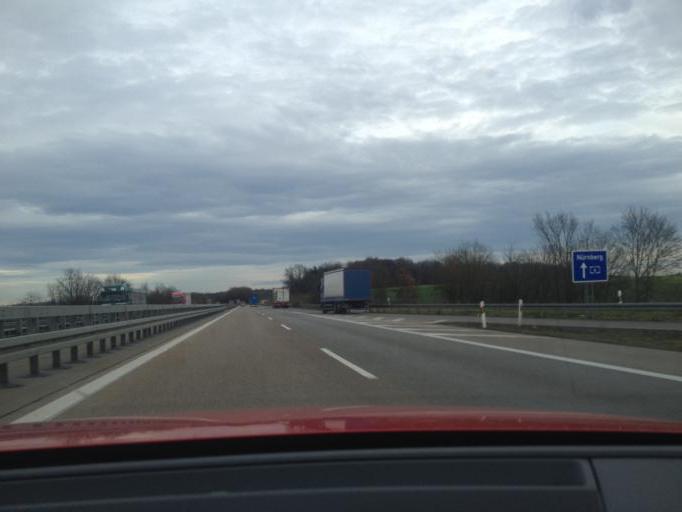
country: DE
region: Baden-Wuerttemberg
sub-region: Regierungsbezirk Stuttgart
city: Kirchberg an der Jagst
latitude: 49.1735
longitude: 9.9971
